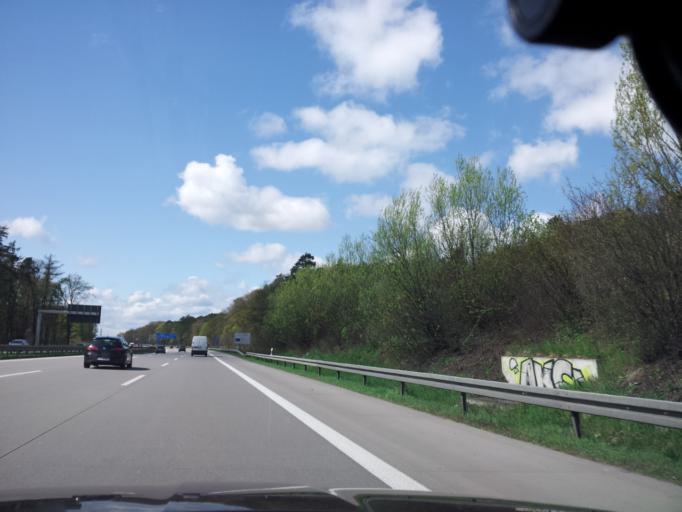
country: DE
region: Brandenburg
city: Ahrensfelde
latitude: 52.6078
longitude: 13.5929
